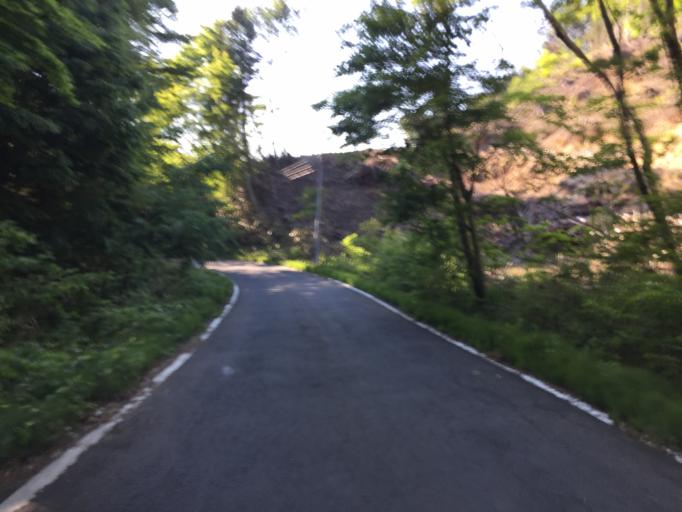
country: JP
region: Ibaraki
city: Kitaibaraki
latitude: 36.8962
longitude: 140.5991
